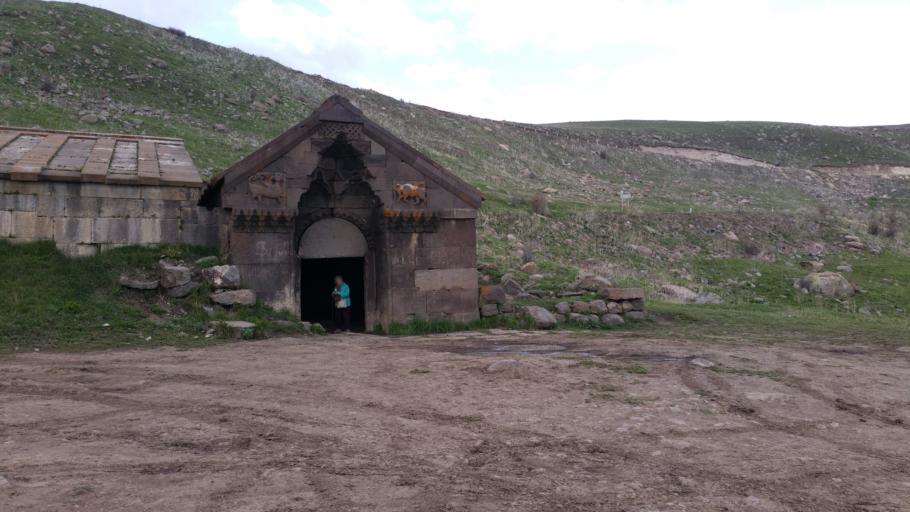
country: AM
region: Geghark'unik'i Marz
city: Madina
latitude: 39.9495
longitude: 45.2363
